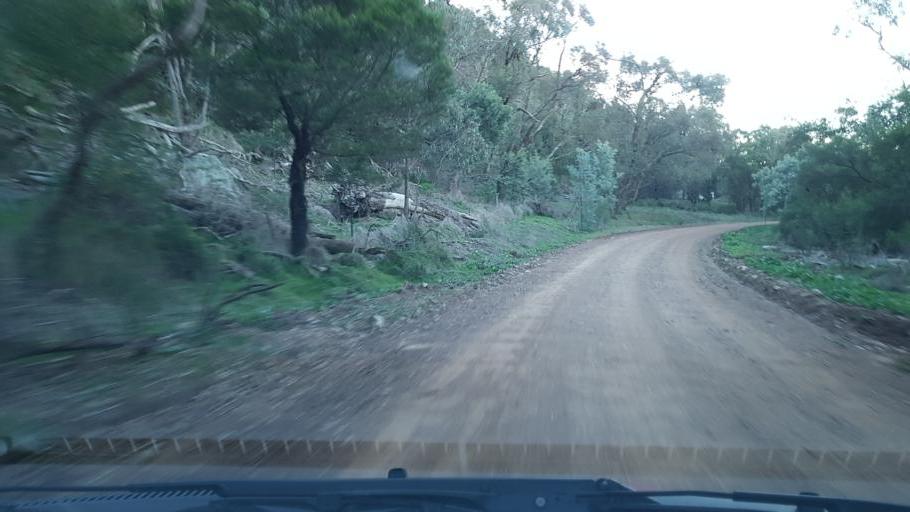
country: AU
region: New South Wales
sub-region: Palerang
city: Bungendore
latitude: -35.1616
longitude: 149.3924
